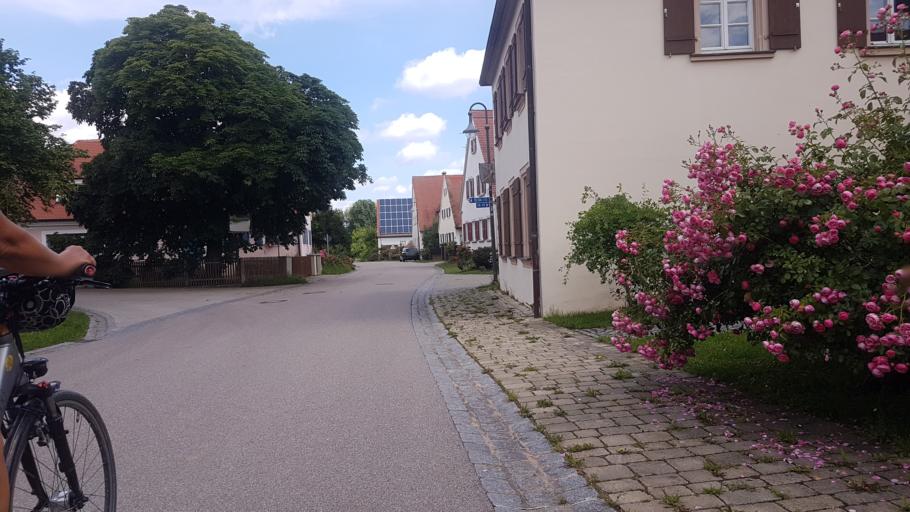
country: DE
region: Bavaria
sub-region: Regierungsbezirk Mittelfranken
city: Dittenheim
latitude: 49.0769
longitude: 10.7980
